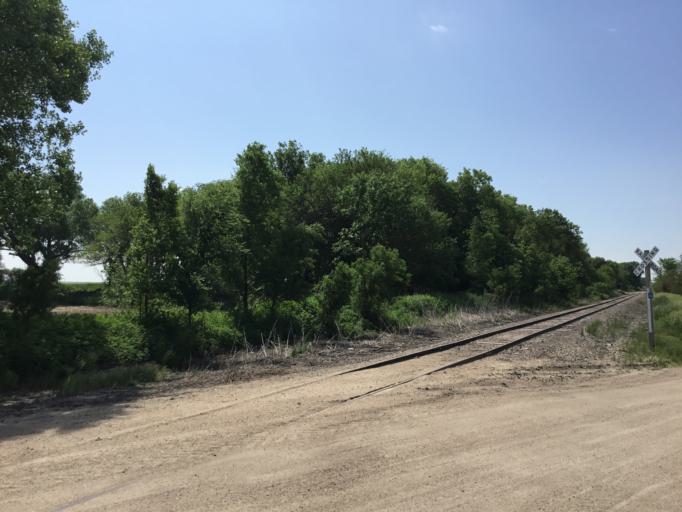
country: US
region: Kansas
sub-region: Republic County
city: Belleville
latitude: 39.7574
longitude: -97.7820
